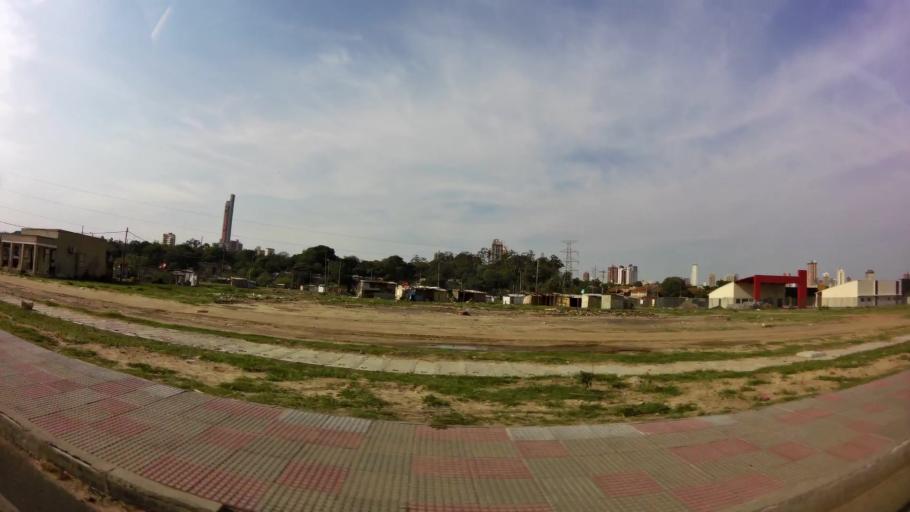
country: PY
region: Asuncion
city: Asuncion
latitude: -25.2769
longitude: -57.6206
